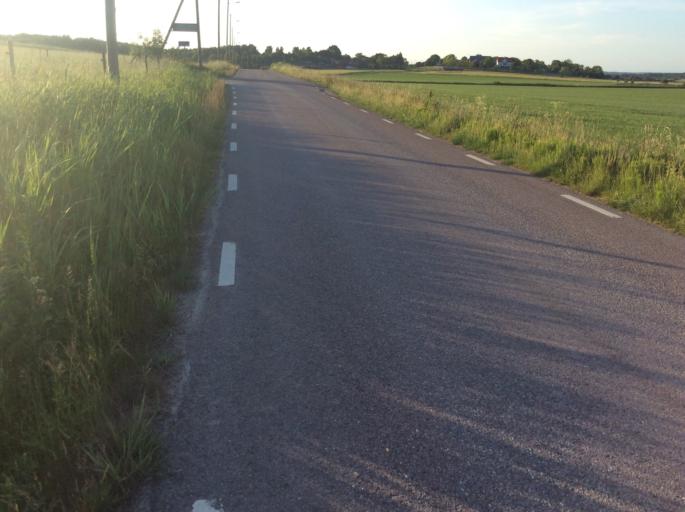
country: SE
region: Vaestra Goetaland
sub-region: Goteborg
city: Majorna
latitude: 57.7941
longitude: 11.8872
